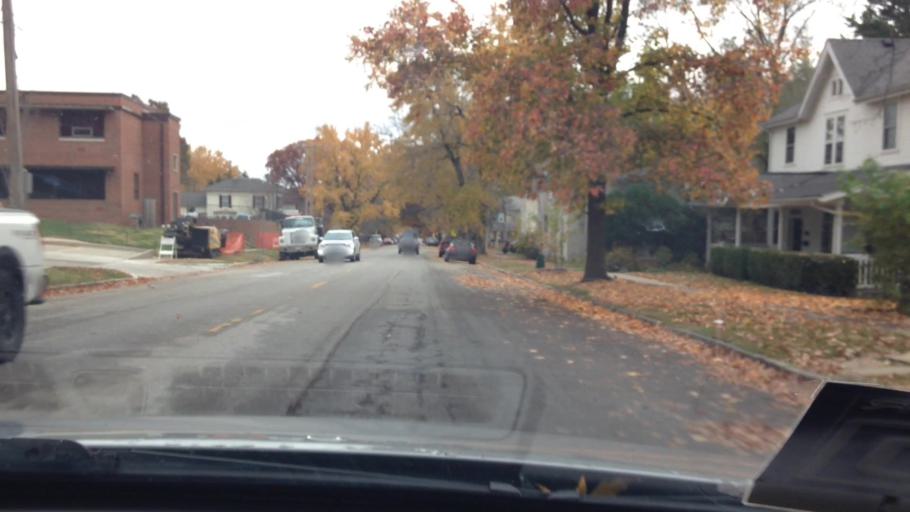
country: US
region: Kansas
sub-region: Leavenworth County
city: Leavenworth
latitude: 39.3065
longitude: -94.9175
